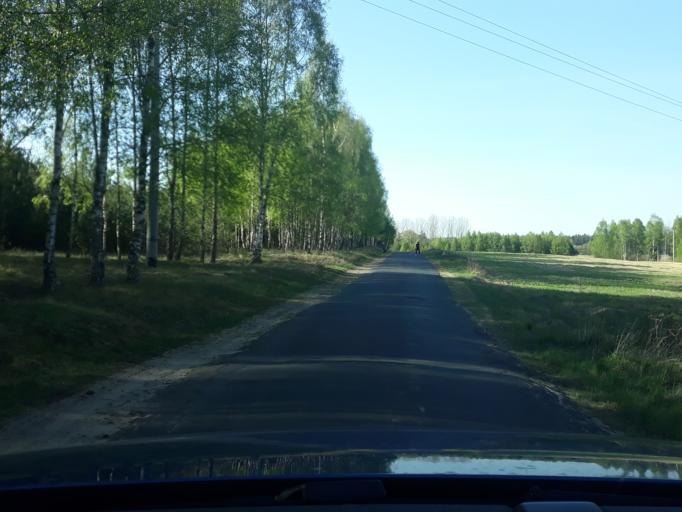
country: PL
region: Pomeranian Voivodeship
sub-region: Powiat czluchowski
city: Przechlewo
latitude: 53.8669
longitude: 17.3342
